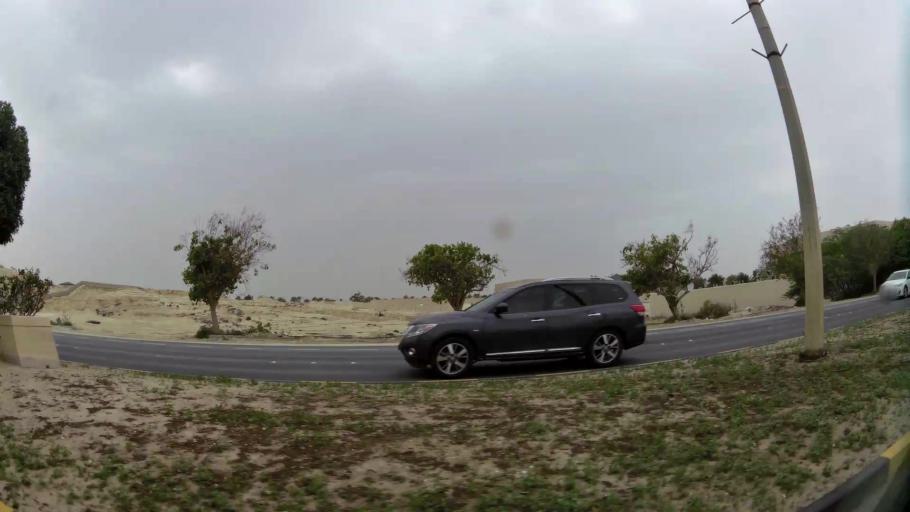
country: BH
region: Northern
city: Ar Rifa'
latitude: 26.1494
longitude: 50.5422
